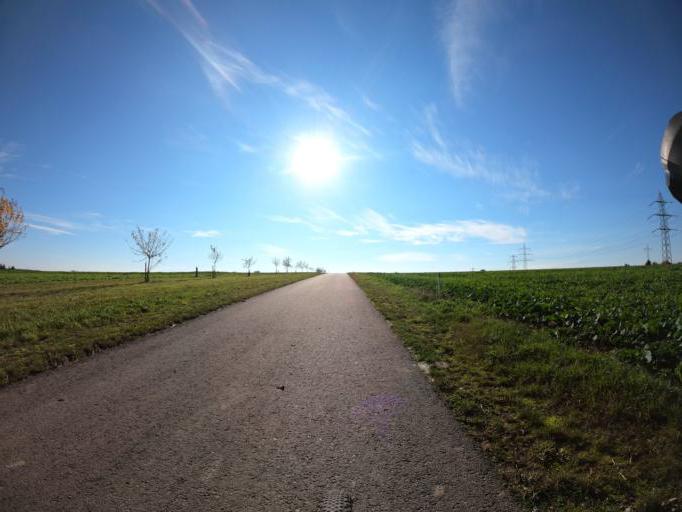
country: DE
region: Baden-Wuerttemberg
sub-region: Regierungsbezirk Stuttgart
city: Magstadt
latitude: 48.7312
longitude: 8.9559
